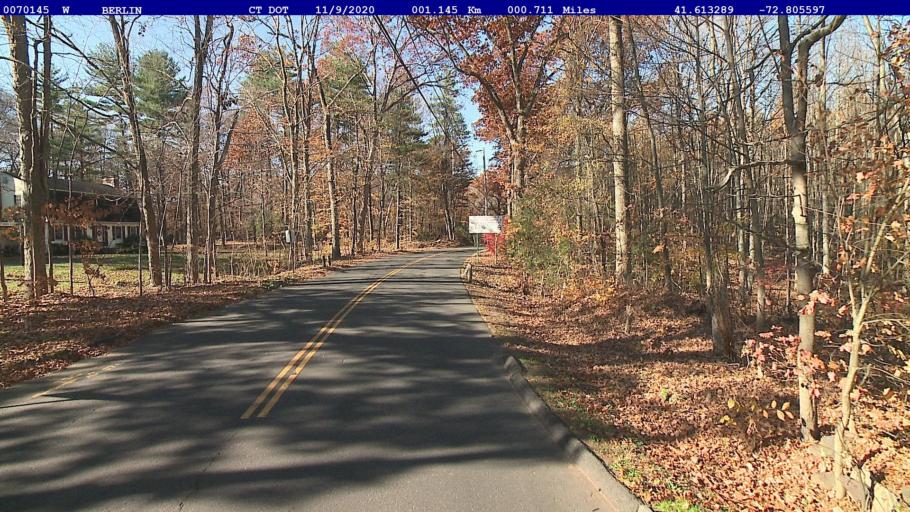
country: US
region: Connecticut
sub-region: Hartford County
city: Kensington
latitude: 41.6133
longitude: -72.8056
